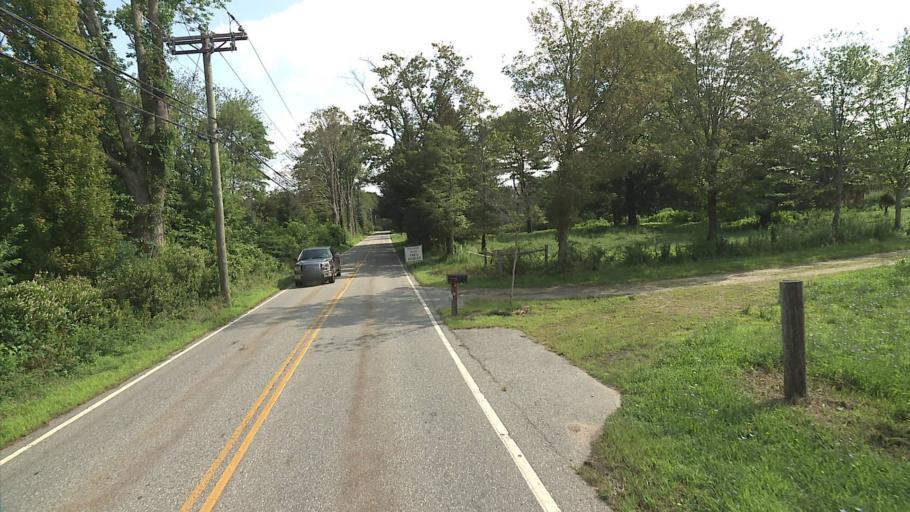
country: US
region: Connecticut
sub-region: Middlesex County
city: Moodus
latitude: 41.5551
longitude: -72.4099
